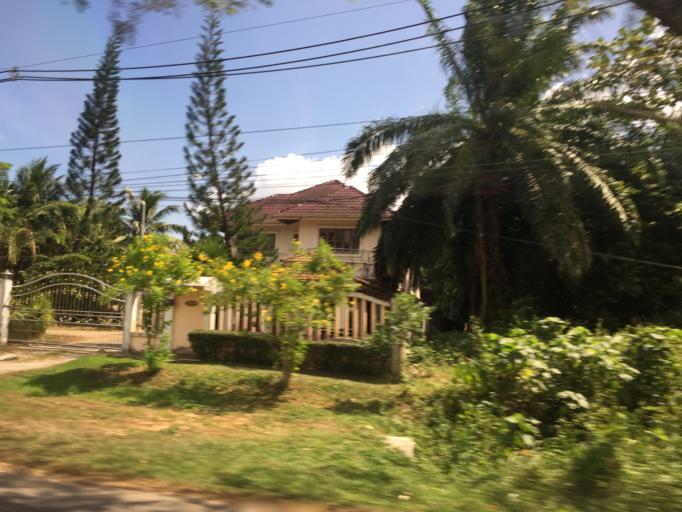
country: TH
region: Krabi
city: Krabi
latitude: 8.0994
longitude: 98.8870
